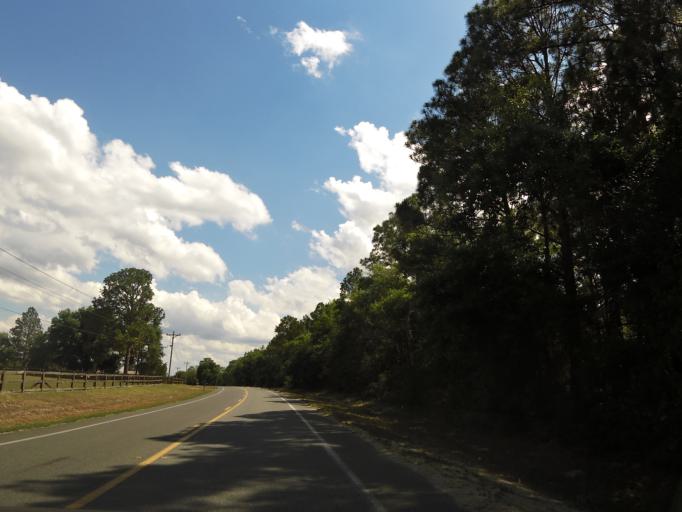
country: US
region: Florida
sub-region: Clay County
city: Keystone Heights
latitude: 29.8388
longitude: -81.9221
